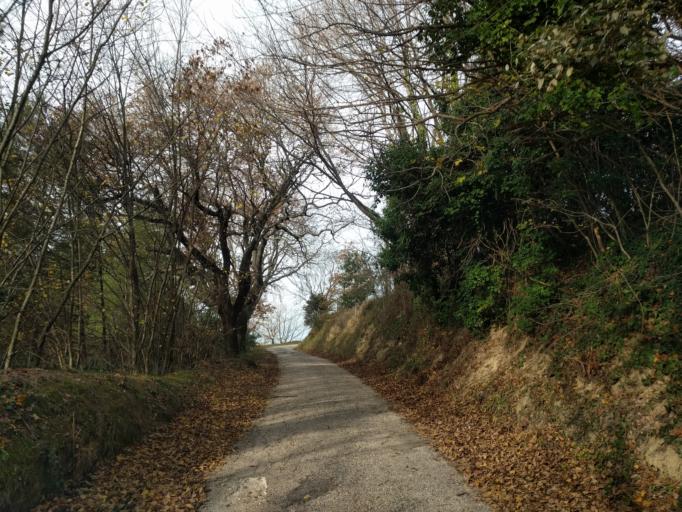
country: IT
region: The Marches
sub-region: Provincia di Pesaro e Urbino
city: Centinarola
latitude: 43.8170
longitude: 12.9726
